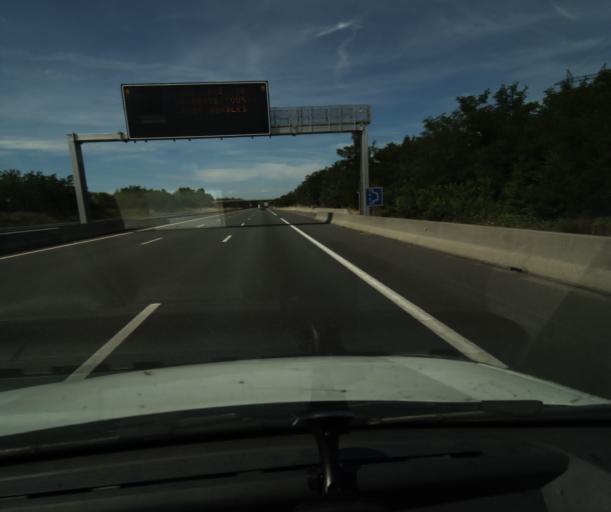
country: FR
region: Midi-Pyrenees
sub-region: Departement du Tarn-et-Garonne
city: Campsas
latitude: 43.8959
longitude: 1.3168
